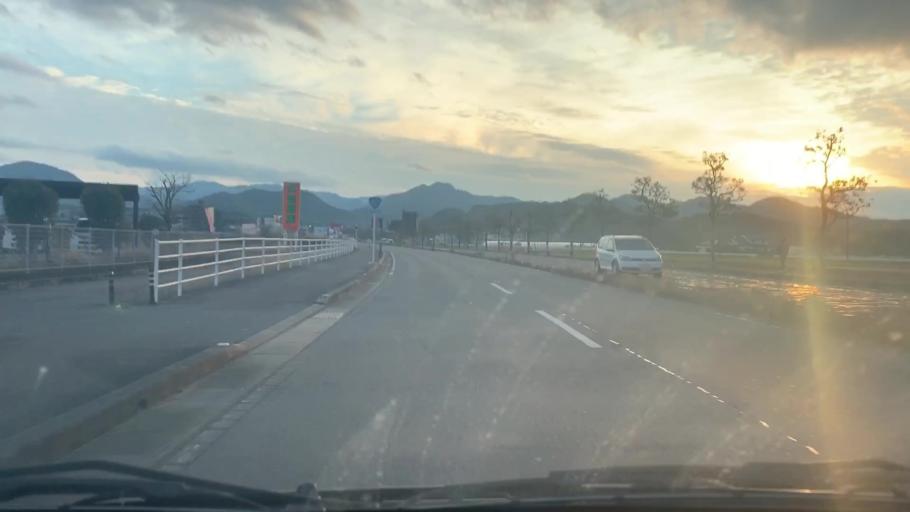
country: JP
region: Saga Prefecture
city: Kashima
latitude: 33.1181
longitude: 130.0903
